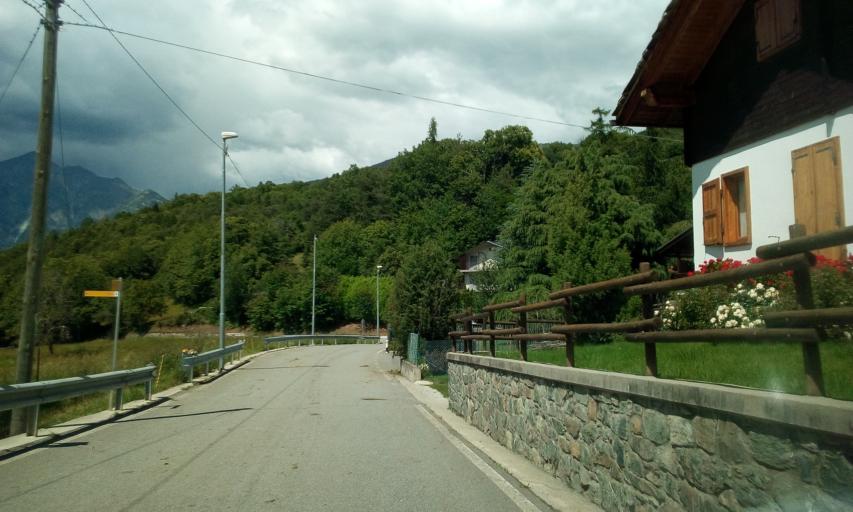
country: IT
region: Aosta Valley
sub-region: Valle d'Aosta
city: Challand-Saint-Victor
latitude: 45.7018
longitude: 7.6926
